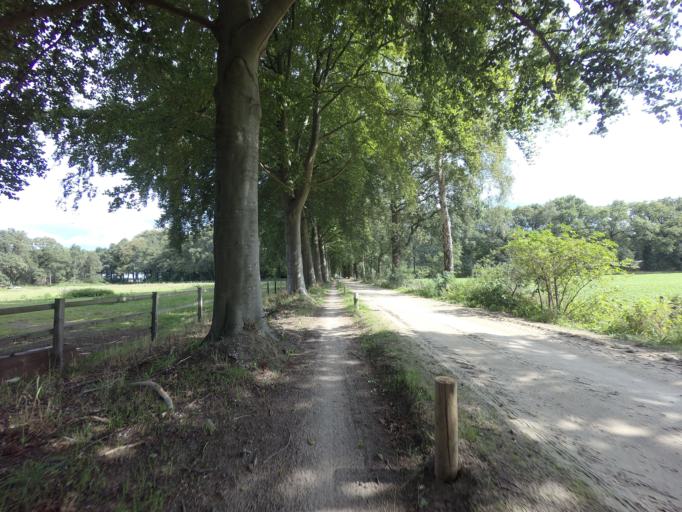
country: NL
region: Overijssel
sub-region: Gemeente Deventer
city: Schalkhaar
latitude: 52.2878
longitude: 6.2450
